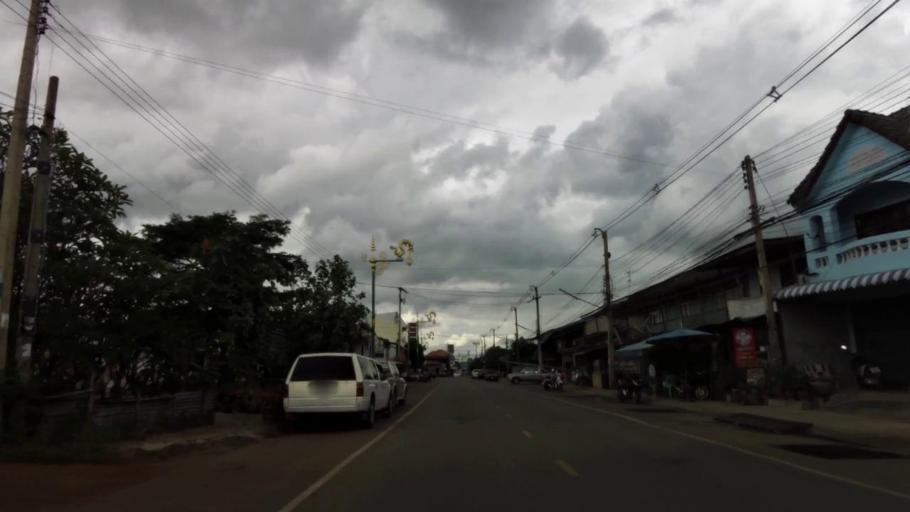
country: TH
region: Nakhon Sawan
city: Phai Sali
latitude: 15.5986
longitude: 100.6486
